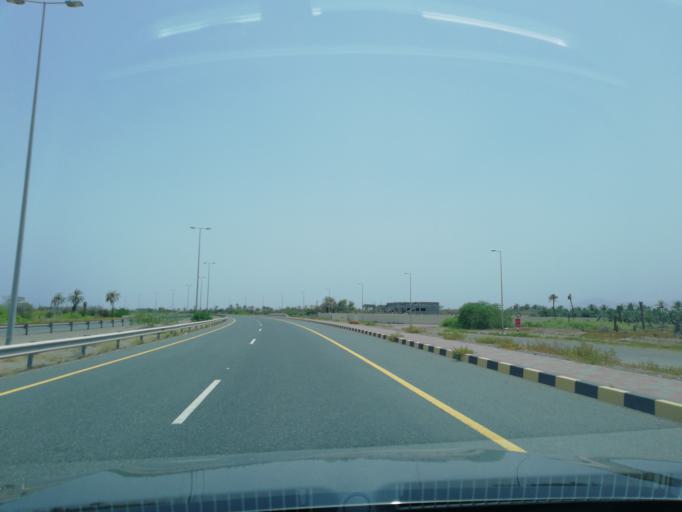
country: OM
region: Al Batinah
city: Shinas
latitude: 24.8393
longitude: 56.4257
